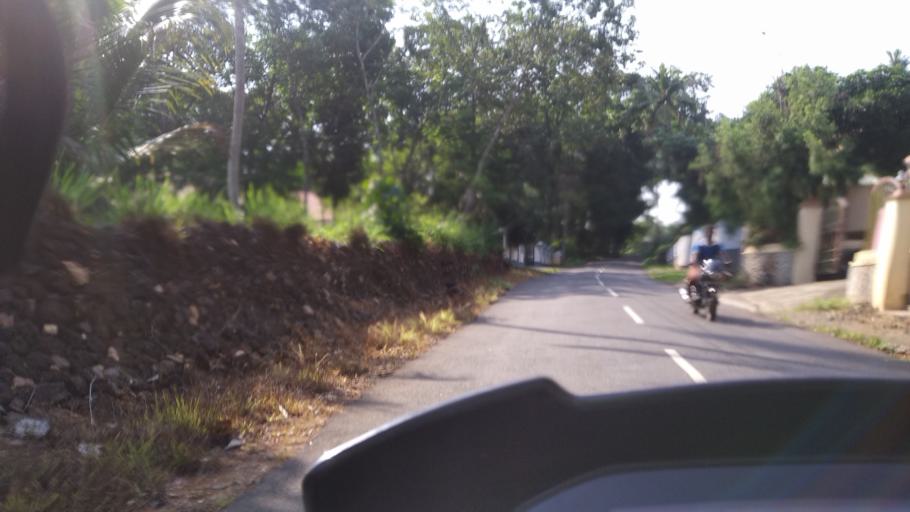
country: IN
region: Kerala
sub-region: Kottayam
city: Palackattumala
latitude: 9.8007
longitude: 76.5835
